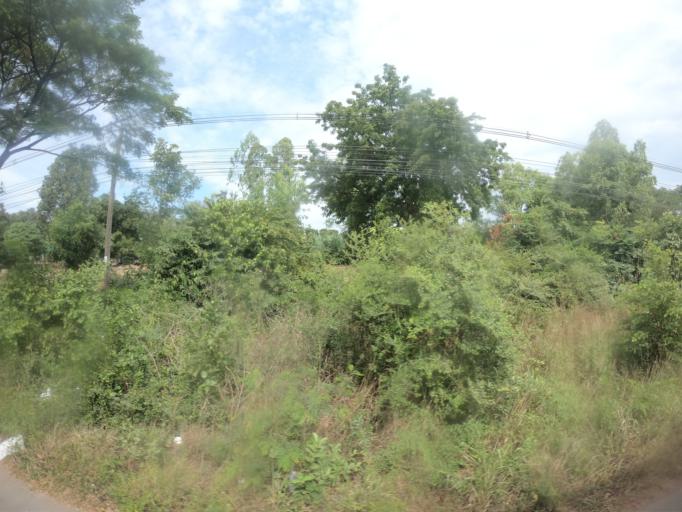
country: TH
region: Maha Sarakham
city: Chiang Yuen
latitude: 16.3432
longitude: 103.1355
